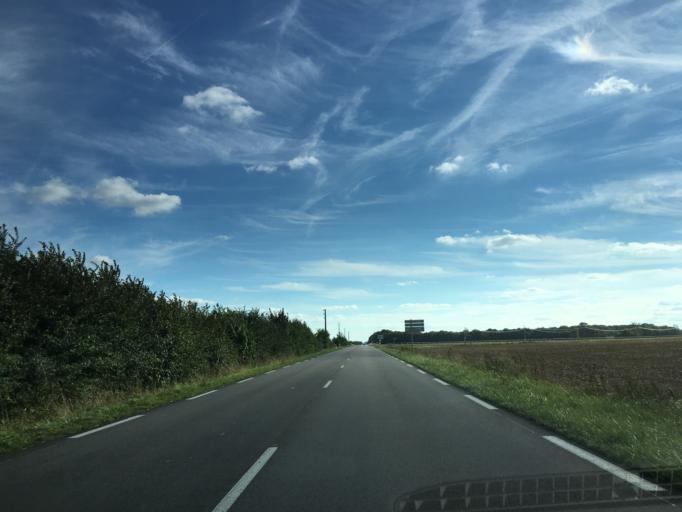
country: FR
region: Lower Normandy
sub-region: Departement du Calvados
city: Orbec
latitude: 48.9487
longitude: 0.4589
